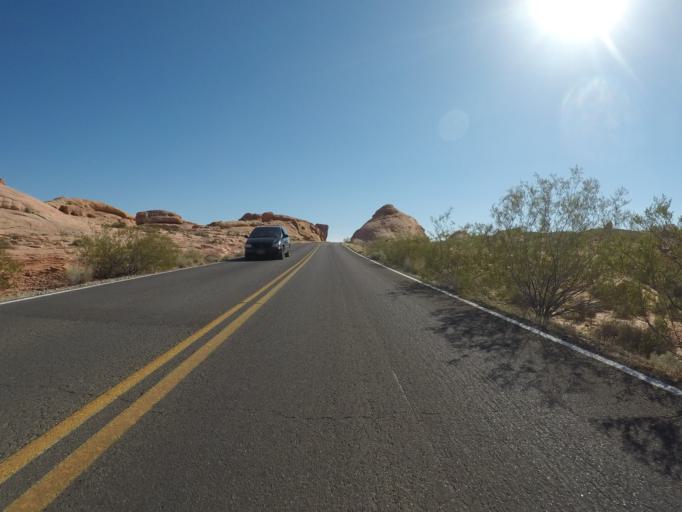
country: US
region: Nevada
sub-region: Clark County
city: Moapa Valley
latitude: 36.4922
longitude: -114.5309
